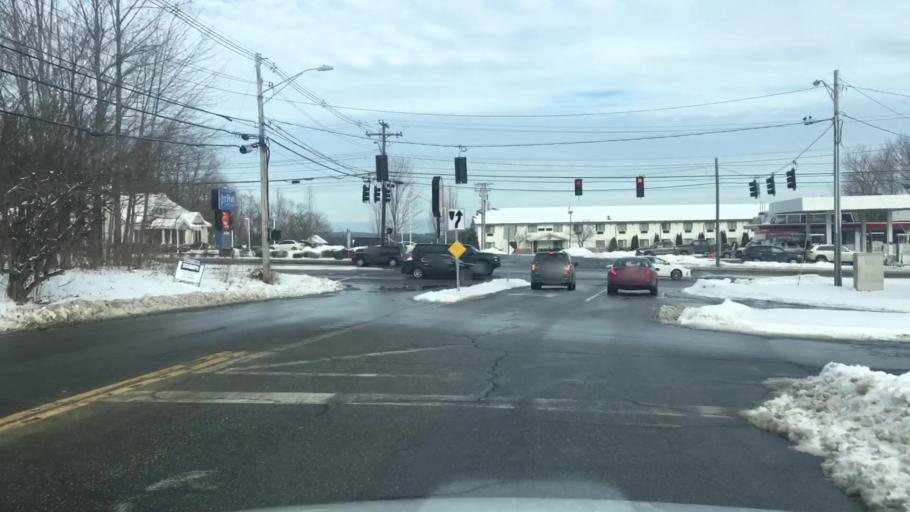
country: US
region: Maine
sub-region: Kennebec County
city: Augusta
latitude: 44.3177
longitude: -69.8169
